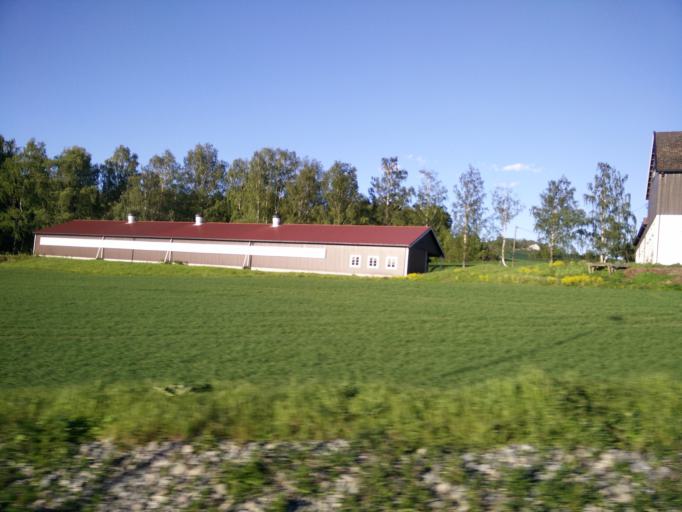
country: NO
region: Buskerud
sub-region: Ringerike
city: Honefoss
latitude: 60.1405
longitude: 10.2630
